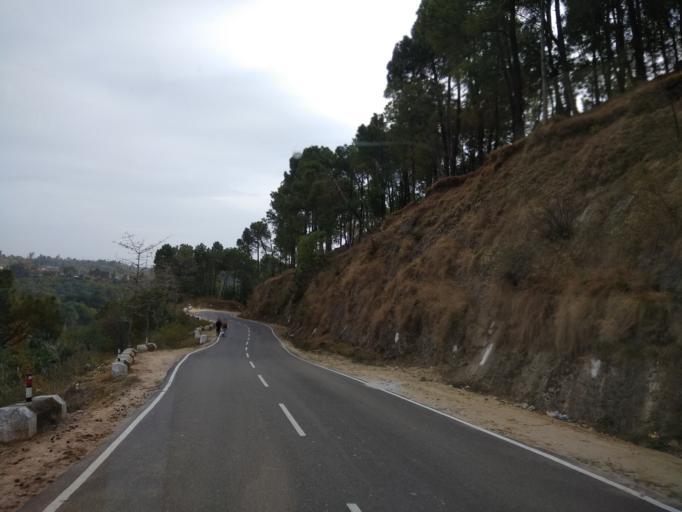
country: IN
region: Himachal Pradesh
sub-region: Kangra
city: Palampur
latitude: 32.1172
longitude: 76.4898
